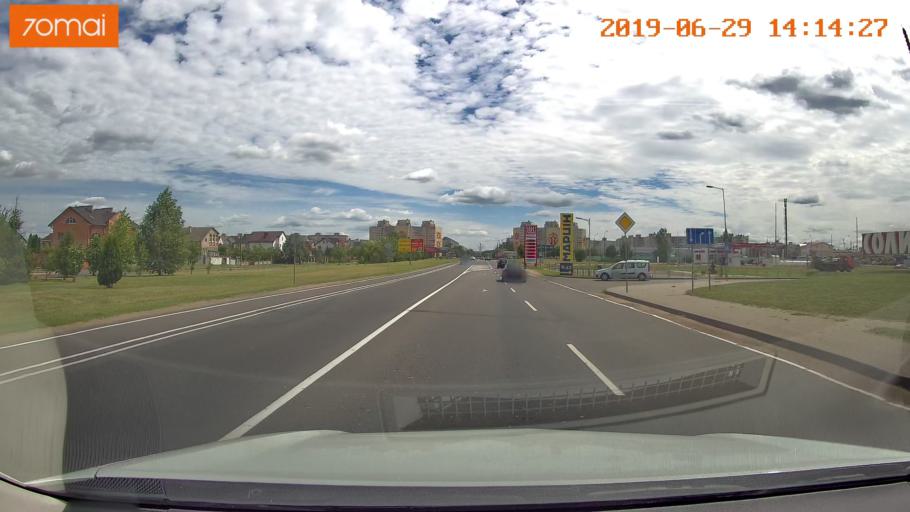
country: BY
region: Minsk
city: Salihorsk
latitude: 52.7957
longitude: 27.5162
